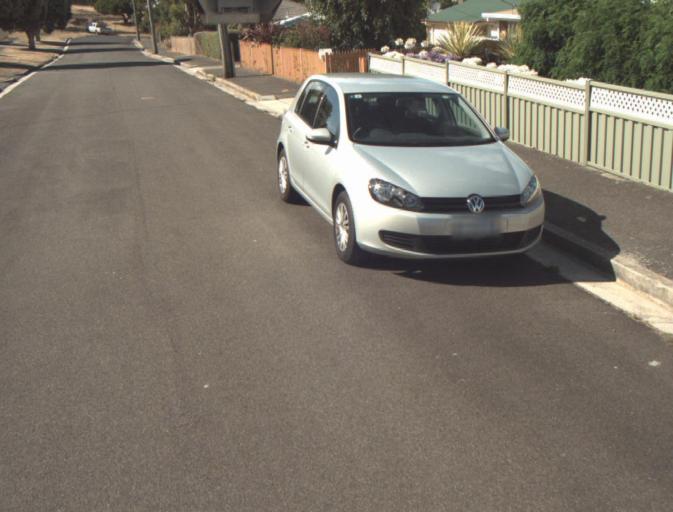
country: AU
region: Tasmania
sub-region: Launceston
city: Newstead
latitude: -41.4262
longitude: 147.1770
